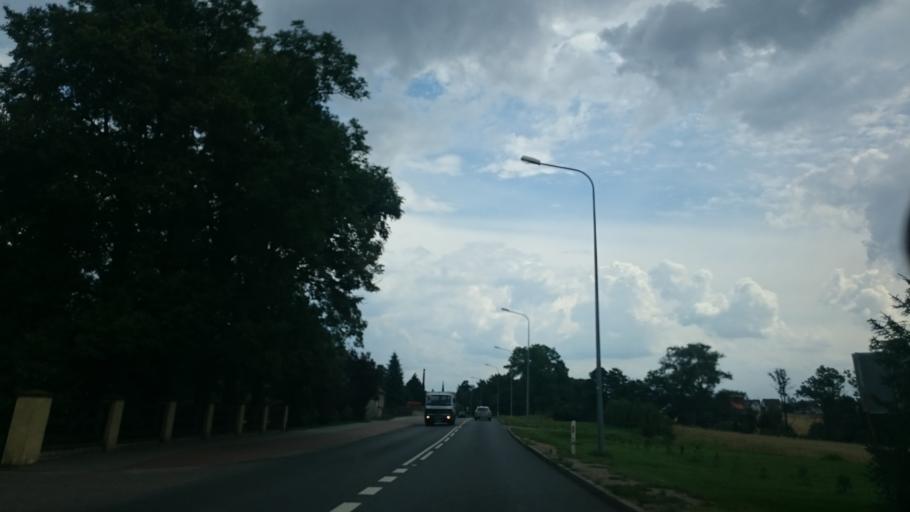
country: PL
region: Kujawsko-Pomorskie
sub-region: Powiat tucholski
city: Kesowo
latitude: 53.6506
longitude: 17.6994
